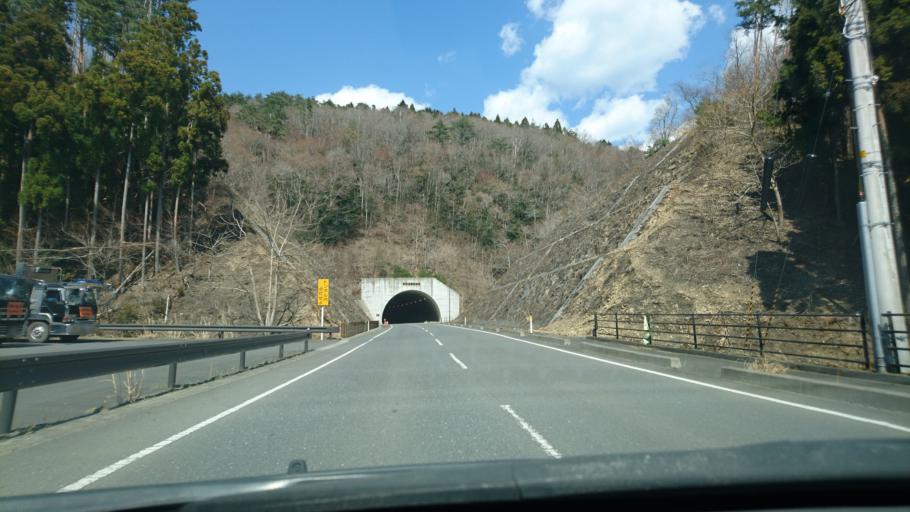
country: JP
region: Miyagi
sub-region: Oshika Gun
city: Onagawa Cho
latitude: 38.4892
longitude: 141.4878
